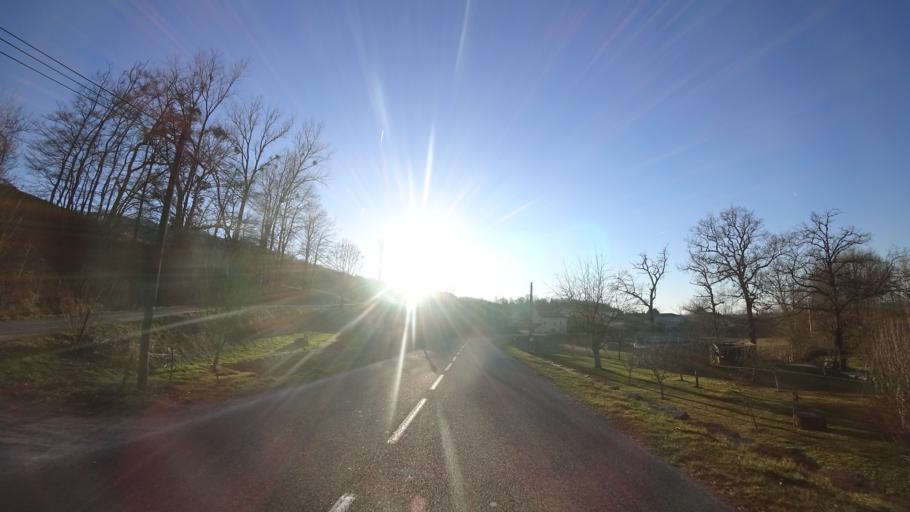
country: FR
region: Midi-Pyrenees
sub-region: Departement de l'Aveyron
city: La Loubiere
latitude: 44.3502
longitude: 2.6859
